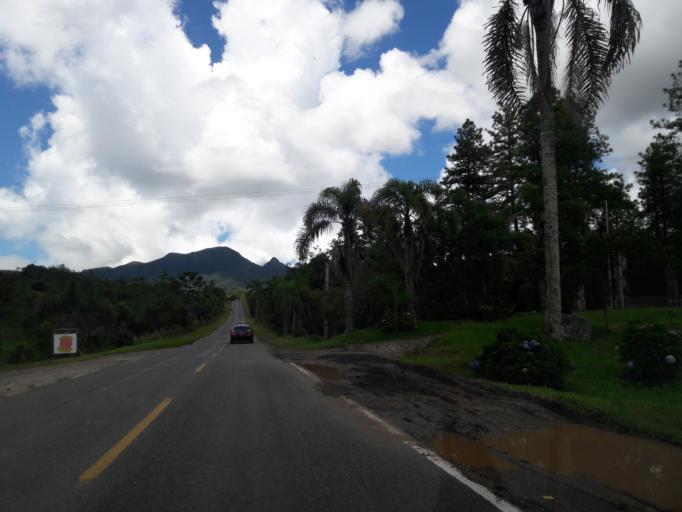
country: BR
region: Parana
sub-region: Campina Grande Do Sul
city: Campina Grande do Sul
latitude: -25.3170
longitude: -48.9290
